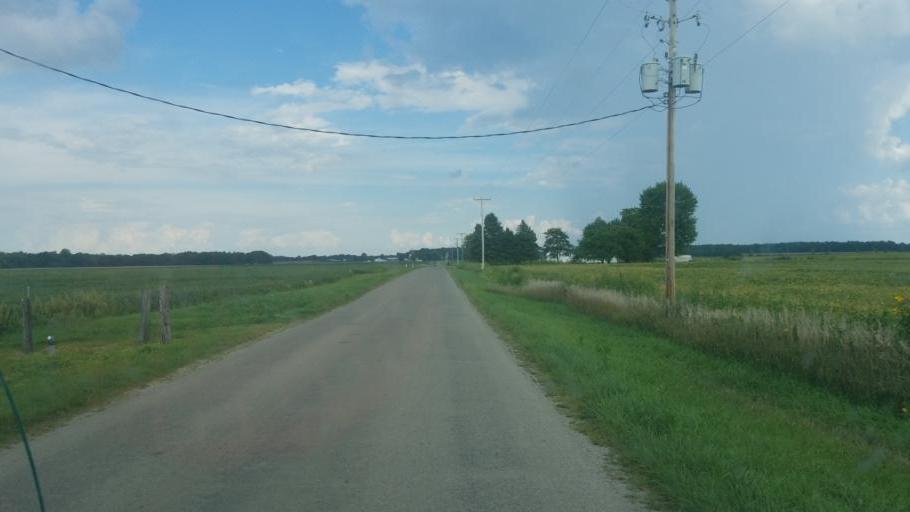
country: US
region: Ohio
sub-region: Huron County
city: Willard
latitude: 41.0187
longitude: -82.7062
